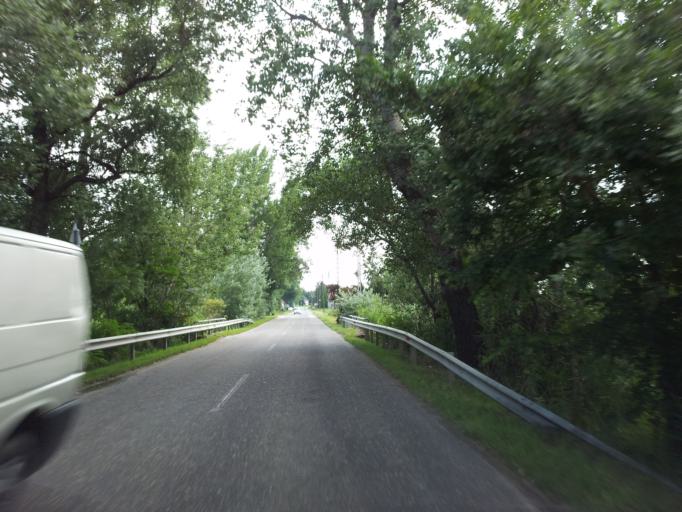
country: HU
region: Pest
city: Szigetcsep
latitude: 47.2743
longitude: 18.9760
